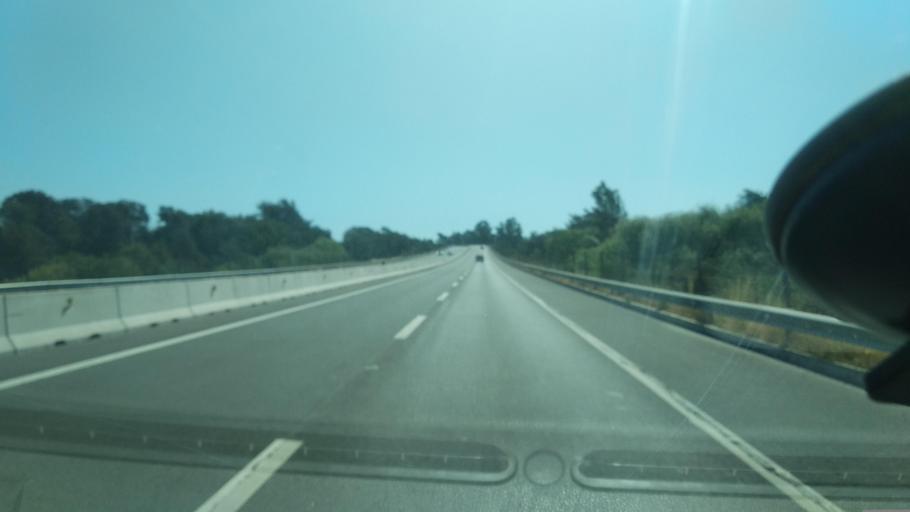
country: CL
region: Valparaiso
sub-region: Provincia de Marga Marga
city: Limache
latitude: -32.9816
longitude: -71.3104
